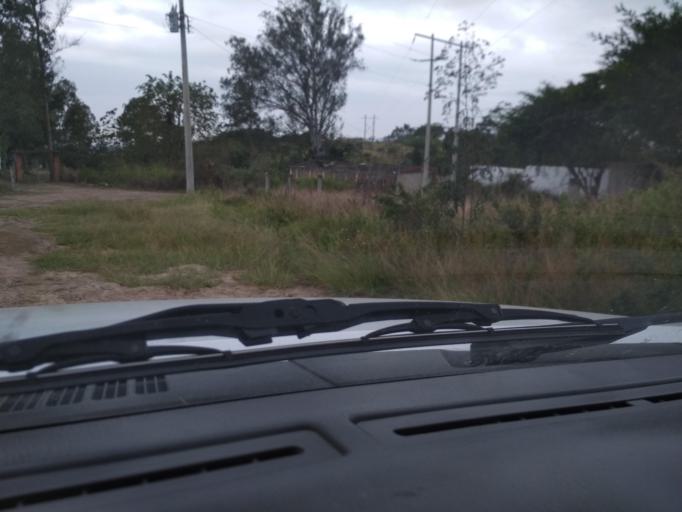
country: MX
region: Veracruz
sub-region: Emiliano Zapata
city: Dos Rios
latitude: 19.5196
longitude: -96.7935
